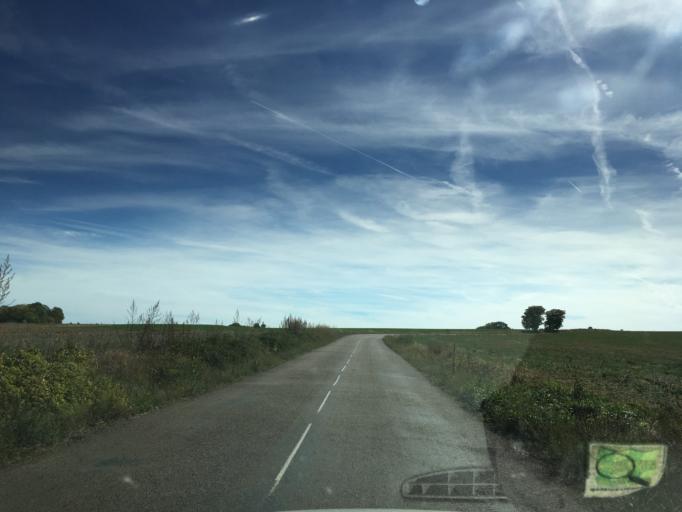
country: FR
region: Bourgogne
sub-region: Departement de l'Yonne
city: Vermenton
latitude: 47.5912
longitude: 3.6987
